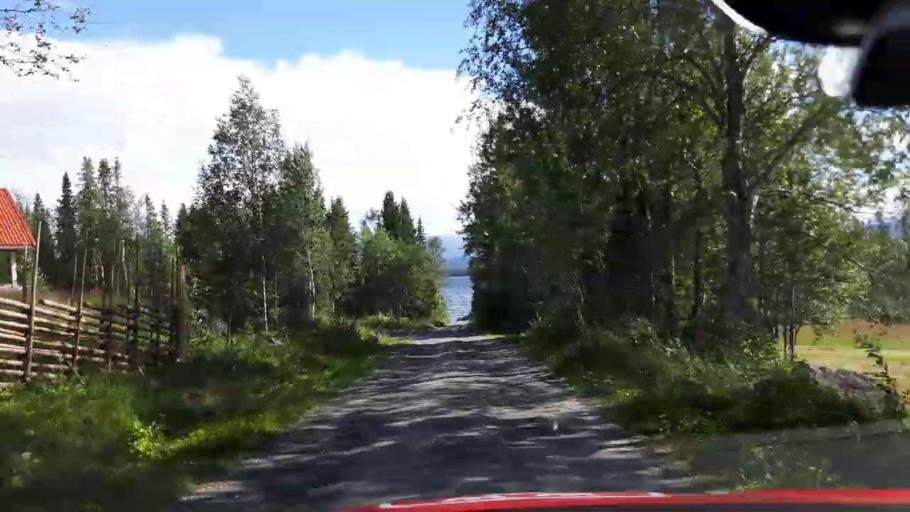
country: SE
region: Jaemtland
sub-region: Are Kommun
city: Are
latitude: 63.2106
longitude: 13.0549
